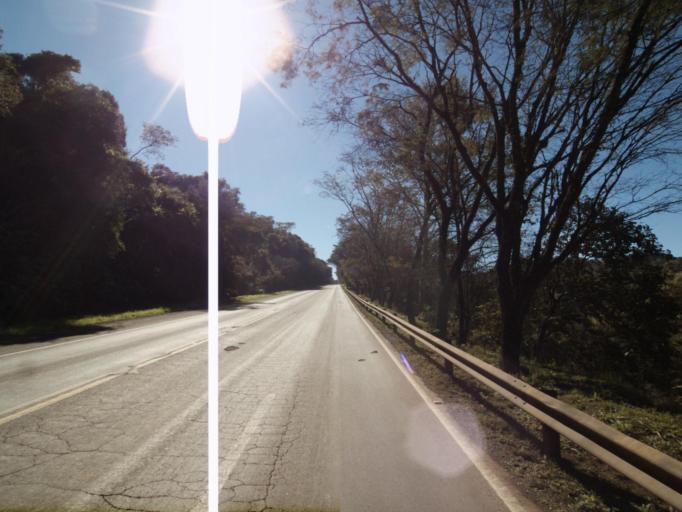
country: BR
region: Rio Grande do Sul
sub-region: Frederico Westphalen
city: Frederico Westphalen
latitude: -26.8023
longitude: -53.3112
